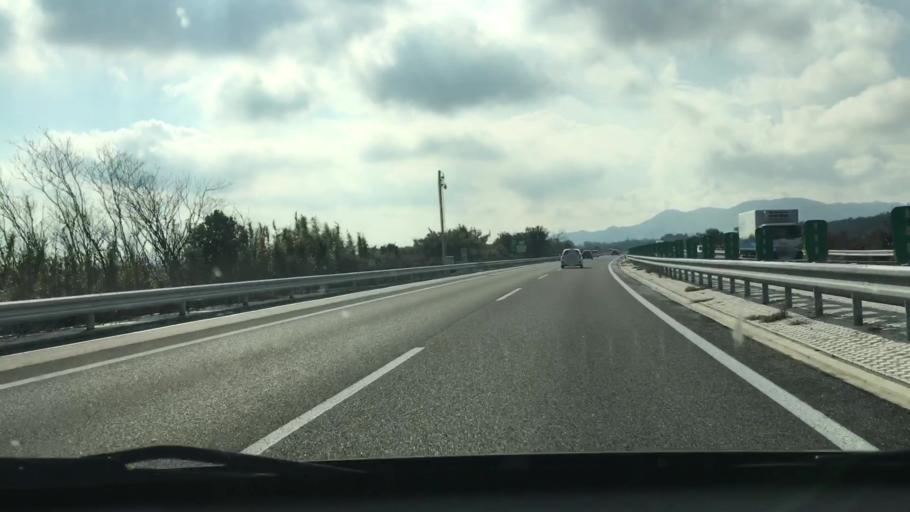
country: JP
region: Kumamoto
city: Uto
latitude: 32.7151
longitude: 130.7665
